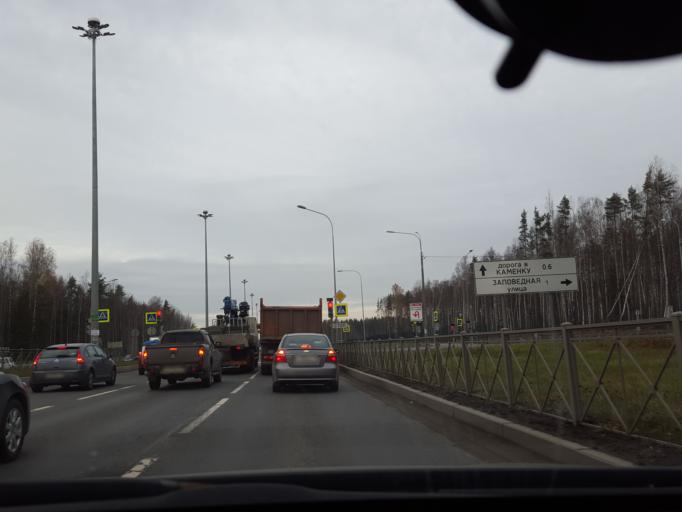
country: RU
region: Leningrad
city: Untolovo
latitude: 60.0476
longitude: 30.2334
